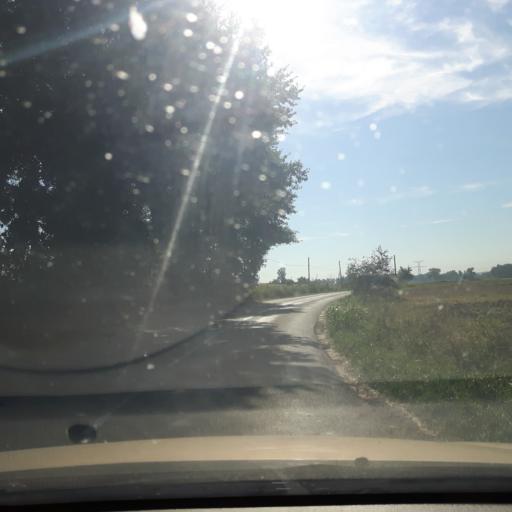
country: FR
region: Midi-Pyrenees
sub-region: Departement de la Haute-Garonne
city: Villeneuve-les-Bouloc
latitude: 43.7619
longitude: 1.4198
